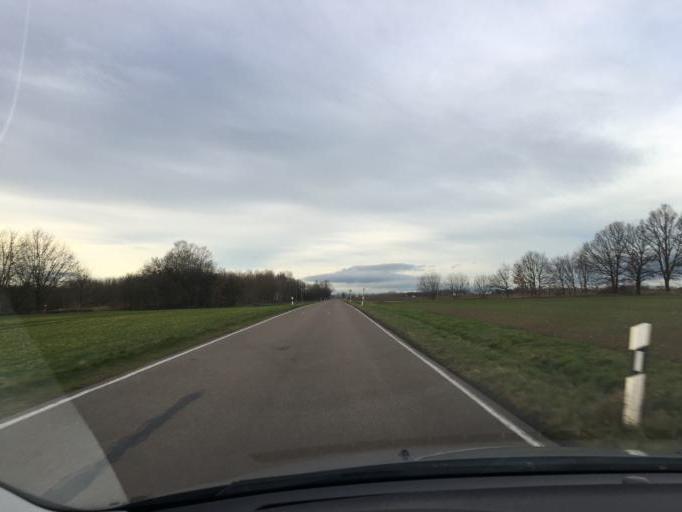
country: DE
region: Saxony
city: Grossposna
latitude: 51.2313
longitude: 12.4942
